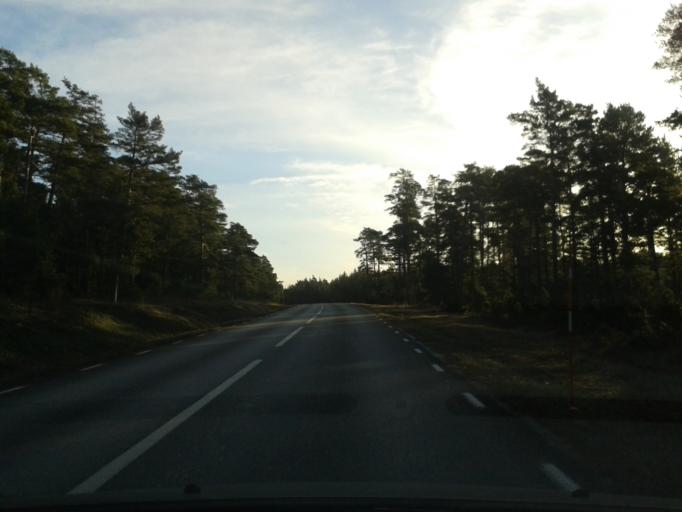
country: SE
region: Gotland
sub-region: Gotland
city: Hemse
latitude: 57.3931
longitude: 18.6449
